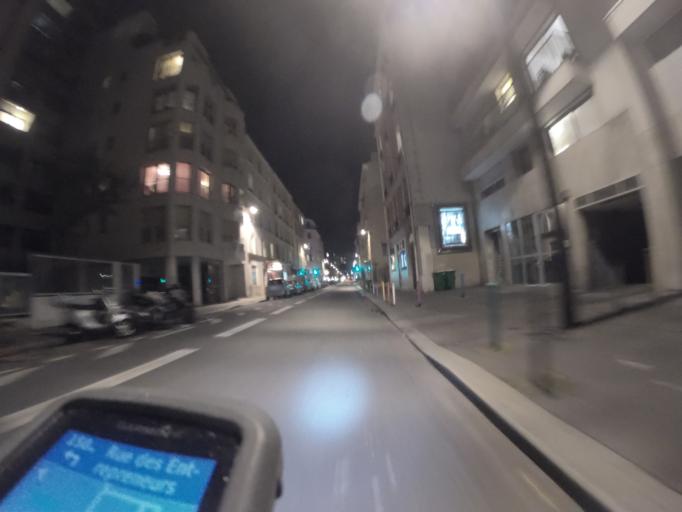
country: FR
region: Ile-de-France
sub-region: Departement des Hauts-de-Seine
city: Vanves
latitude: 48.8462
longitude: 2.2884
